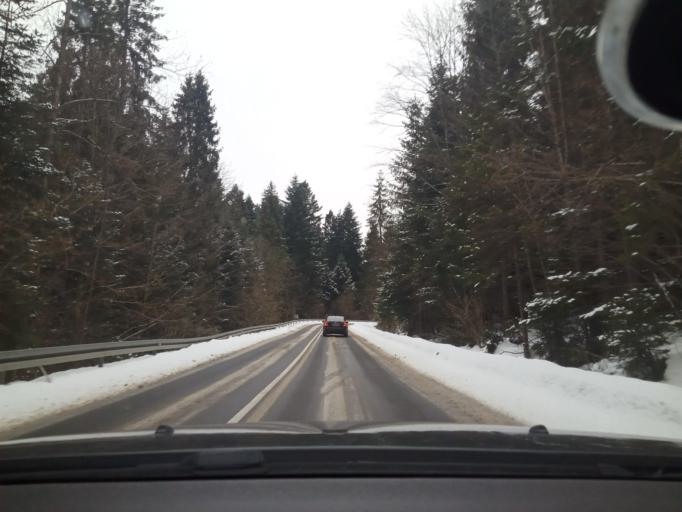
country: PL
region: Lesser Poland Voivodeship
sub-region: Powiat nowotarski
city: Krosnica
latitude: 49.4254
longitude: 20.3473
